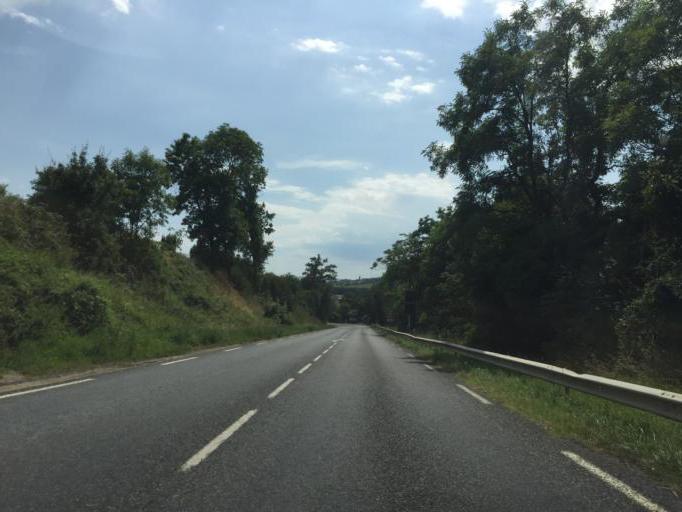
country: FR
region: Rhone-Alpes
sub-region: Departement du Rhone
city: Bully
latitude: 45.8461
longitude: 4.5798
